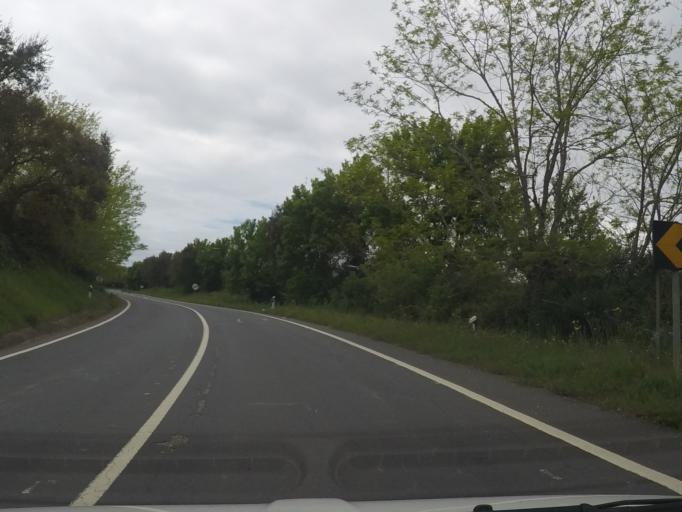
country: PT
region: Setubal
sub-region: Santiago do Cacem
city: Cercal
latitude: 37.8292
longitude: -8.6981
